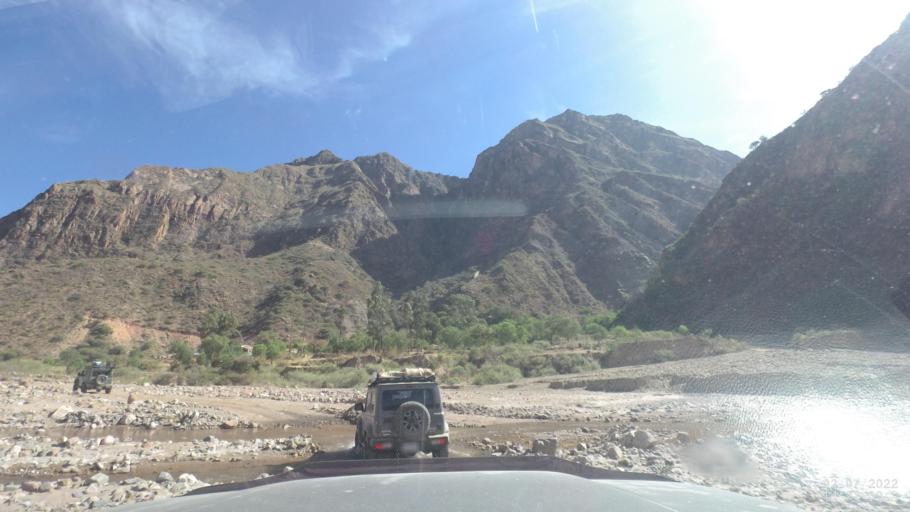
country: BO
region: Cochabamba
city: Irpa Irpa
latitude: -17.8299
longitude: -66.4136
